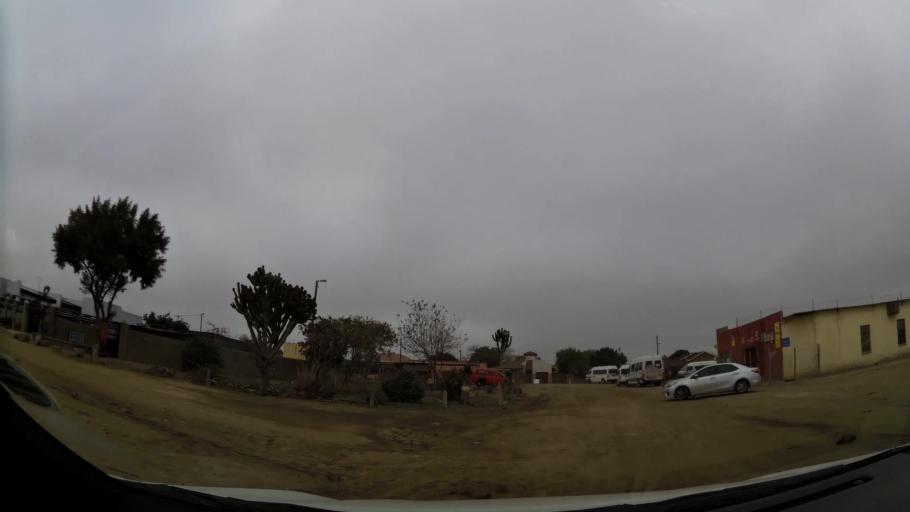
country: ZA
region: Limpopo
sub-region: Capricorn District Municipality
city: Polokwane
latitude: -23.8343
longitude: 29.3892
